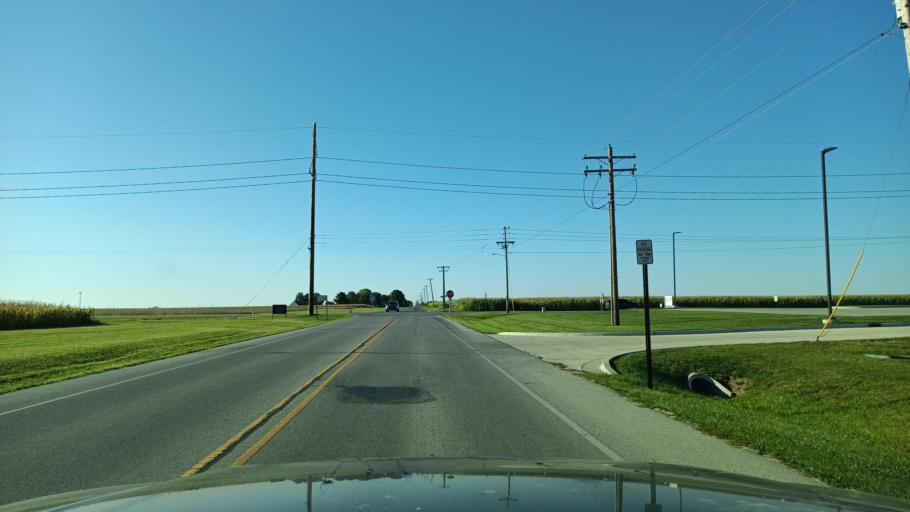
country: US
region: Illinois
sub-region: Champaign County
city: Savoy
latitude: 40.0553
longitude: -88.2383
